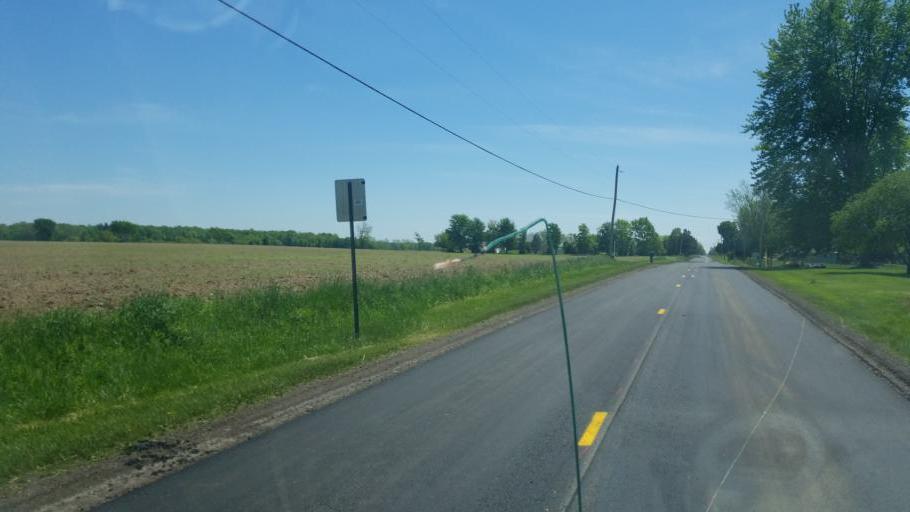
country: US
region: Ohio
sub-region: Huron County
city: Norwalk
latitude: 41.2045
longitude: -82.5903
